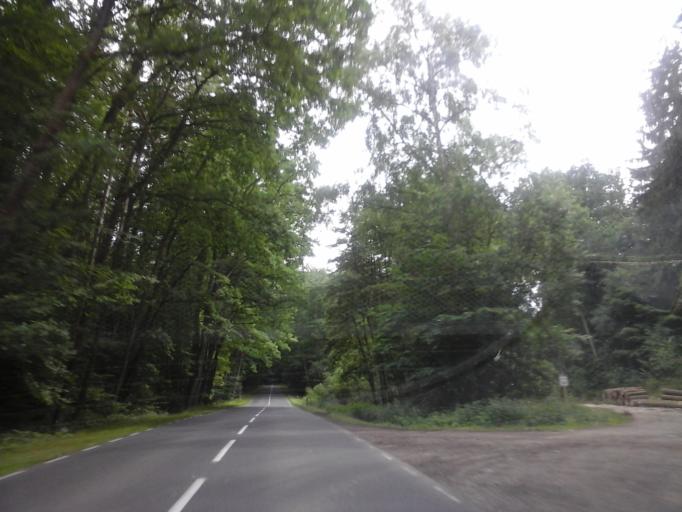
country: PL
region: West Pomeranian Voivodeship
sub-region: Powiat stargardzki
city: Suchan
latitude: 53.2691
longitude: 15.3290
